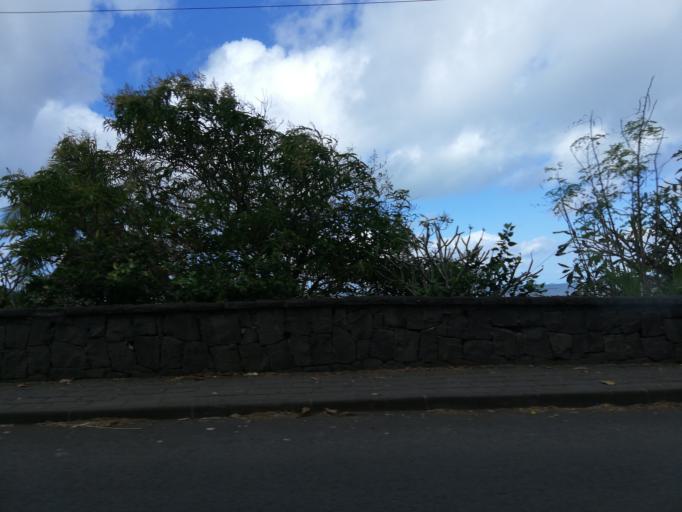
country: MU
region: Grand Port
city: Bambous Virieux
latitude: -20.3455
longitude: 57.7650
